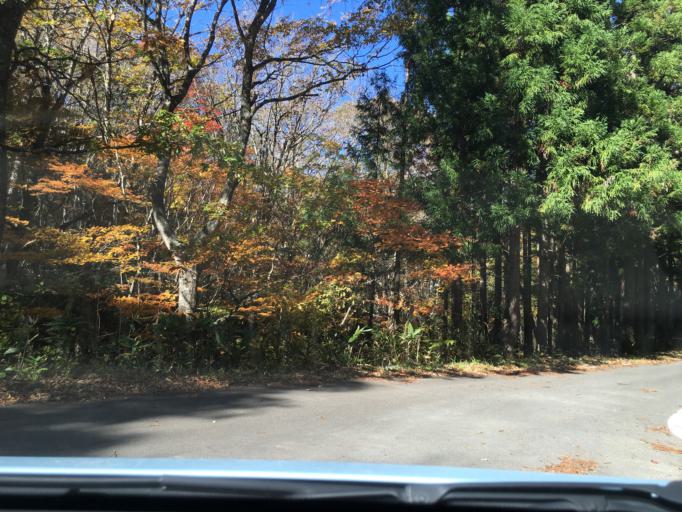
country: JP
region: Fukushima
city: Inawashiro
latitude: 37.3971
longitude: 140.0157
